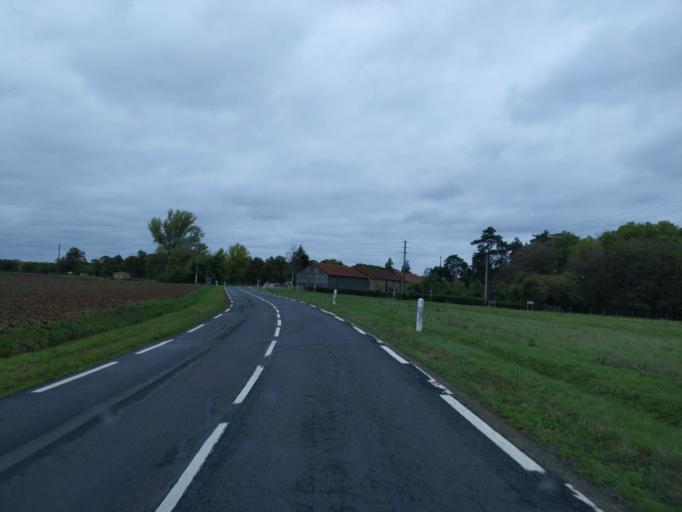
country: FR
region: Ile-de-France
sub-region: Departement des Yvelines
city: Bullion
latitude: 48.6421
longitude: 1.9863
